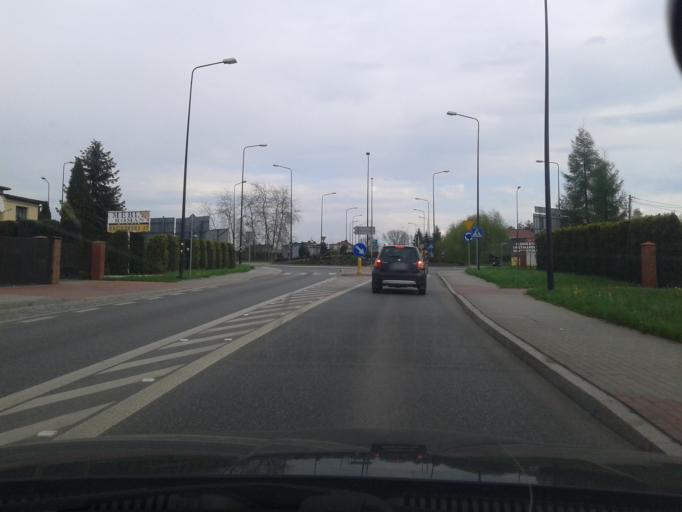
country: PL
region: Silesian Voivodeship
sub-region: Powiat rybnicki
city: Swierklany Gorne
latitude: 50.0836
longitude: 18.5989
